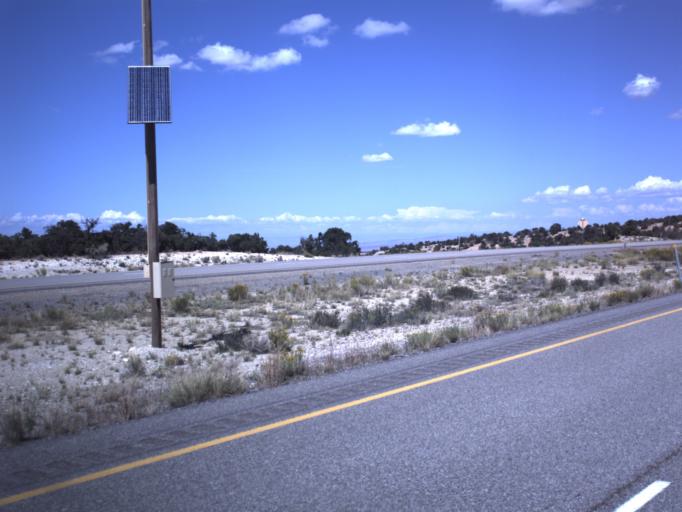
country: US
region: Utah
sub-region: Emery County
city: Ferron
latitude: 38.8511
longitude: -110.9269
